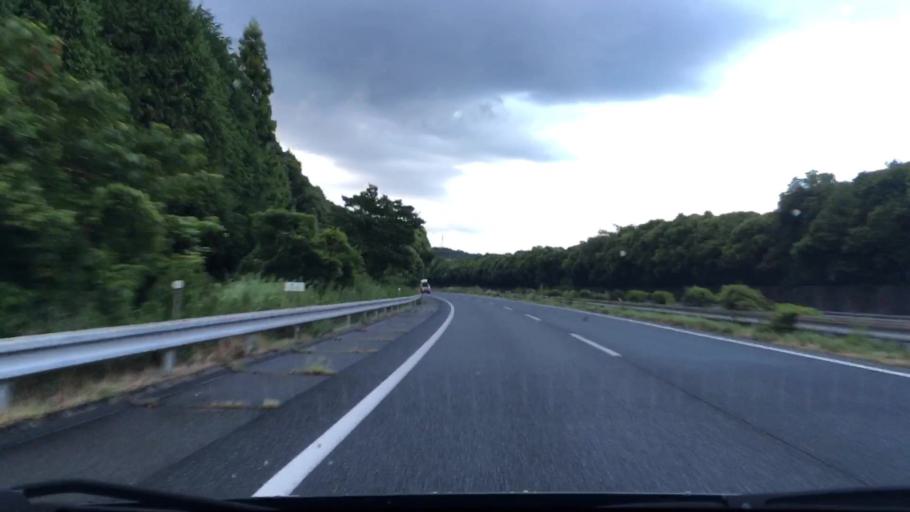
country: JP
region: Yamaguchi
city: Shimonoseki
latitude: 33.8769
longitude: 130.9691
